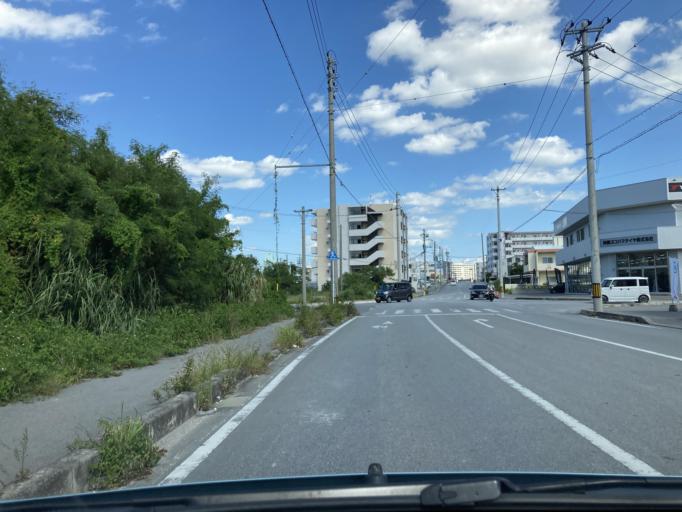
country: JP
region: Okinawa
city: Tomigusuku
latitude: 26.1906
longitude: 127.7118
